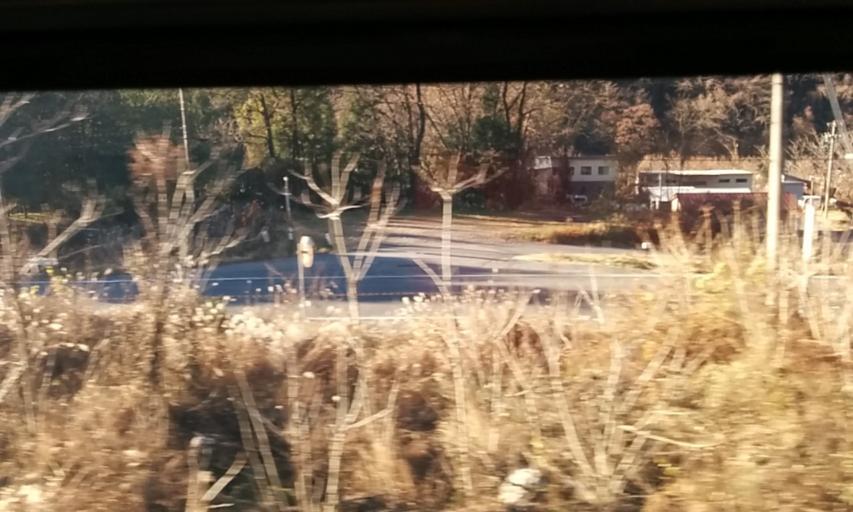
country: JP
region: Nagano
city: Iida
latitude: 35.7053
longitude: 137.7019
